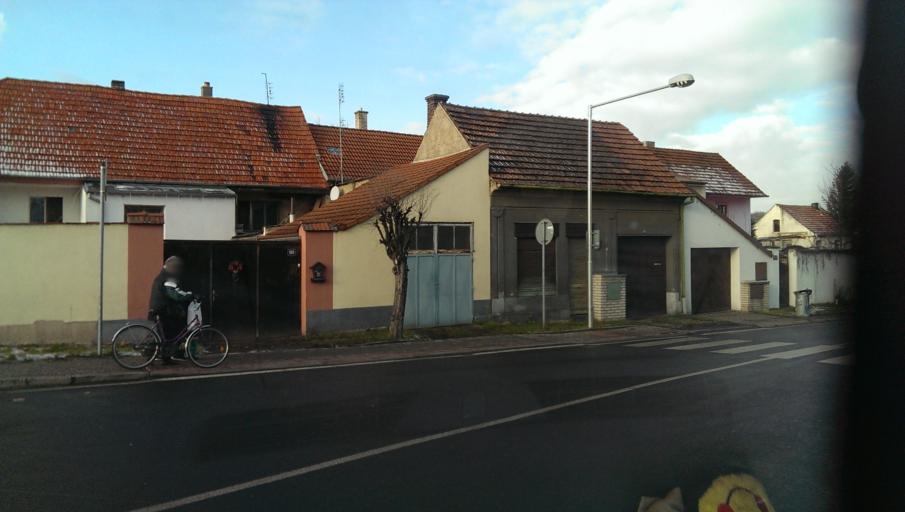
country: CZ
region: Ustecky
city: Budyne nad Ohri
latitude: 50.4045
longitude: 14.1288
